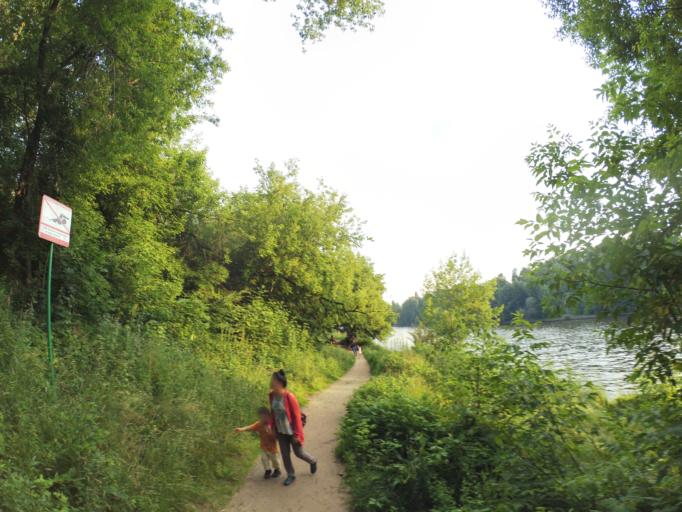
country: RU
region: Moscow
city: Shchukino
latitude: 55.7887
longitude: 37.4468
